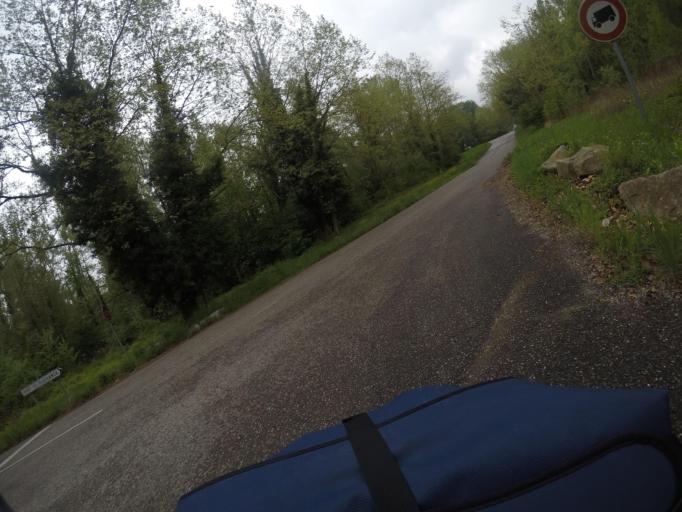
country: DE
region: Baden-Wuerttemberg
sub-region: Karlsruhe Region
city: Iffezheim
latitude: 48.8430
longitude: 8.1048
